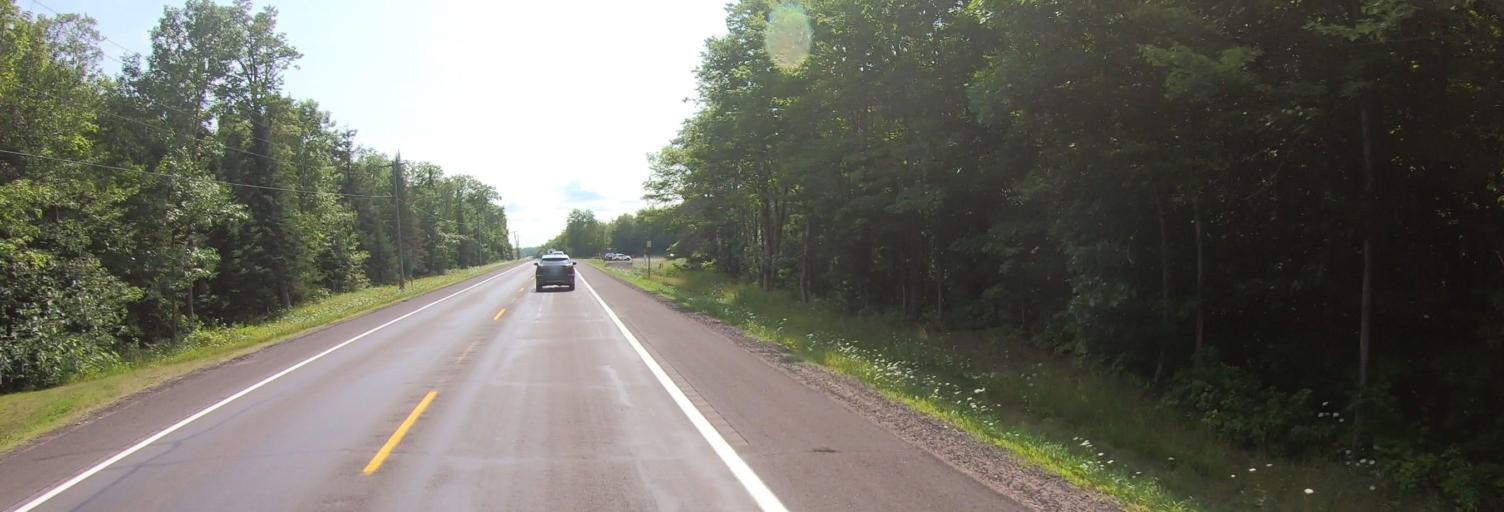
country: US
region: Michigan
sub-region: Houghton County
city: Hancock
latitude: 46.8888
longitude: -88.8599
